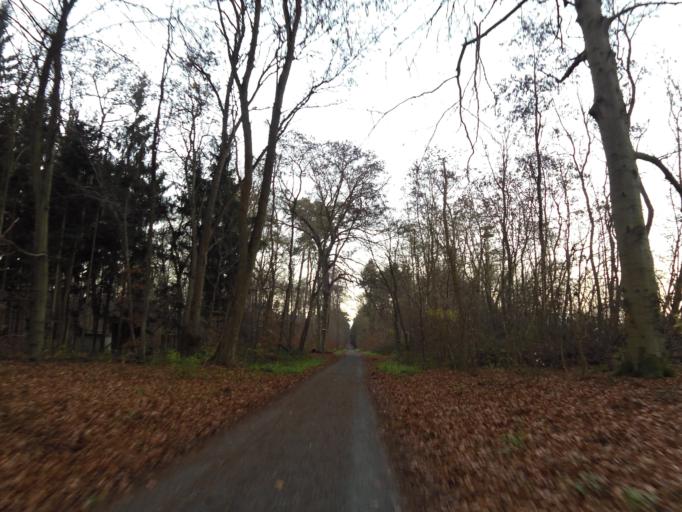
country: DE
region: Hesse
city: Morfelden-Walldorf
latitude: 50.0004
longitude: 8.5959
